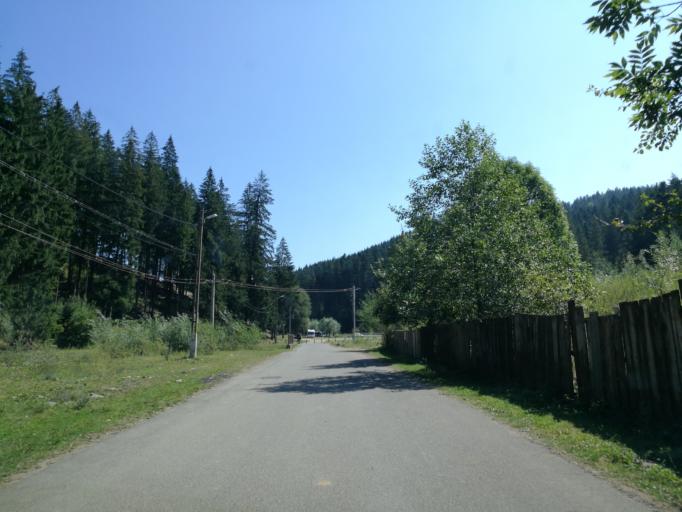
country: RO
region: Suceava
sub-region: Comuna Putna
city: Putna
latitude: 47.8655
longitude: 25.6160
